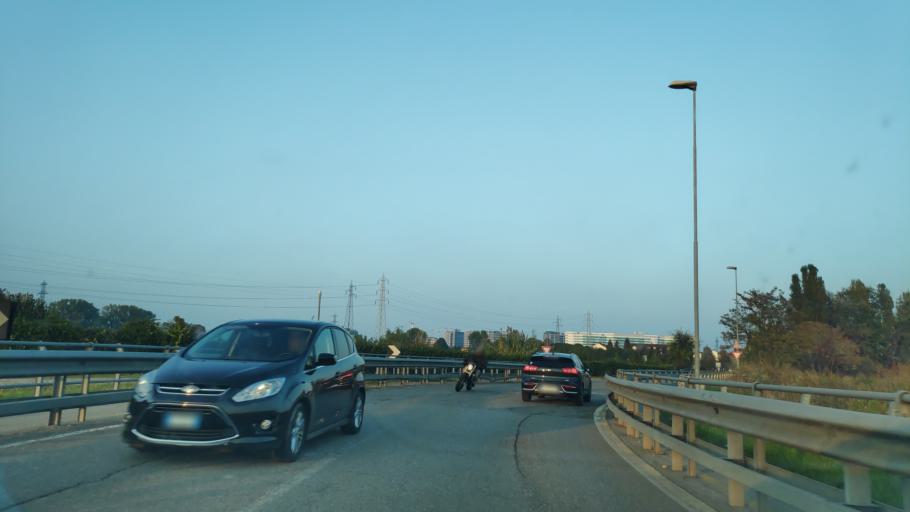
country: IT
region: Lombardy
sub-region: Citta metropolitana di Milano
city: Chiaravalle
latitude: 45.4111
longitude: 9.2471
